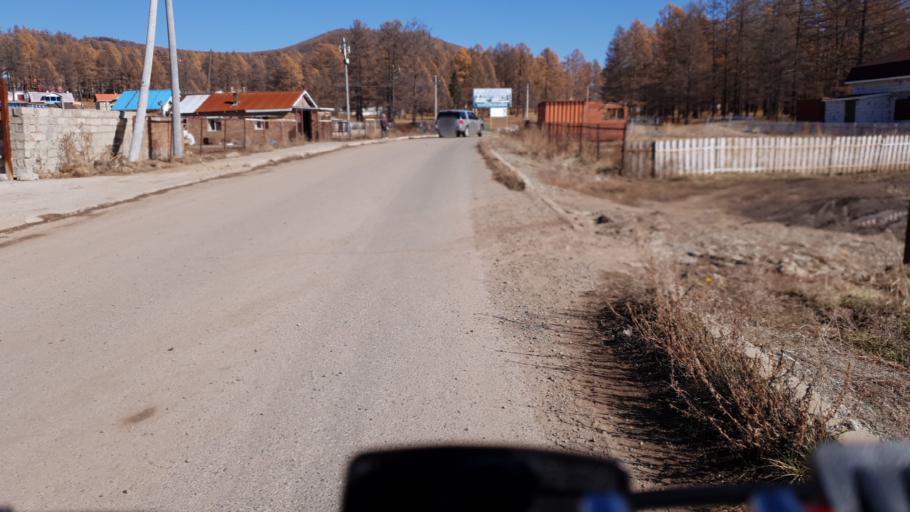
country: MN
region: Ulaanbaatar
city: Ulaanbaatar
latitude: 48.1140
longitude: 106.9165
